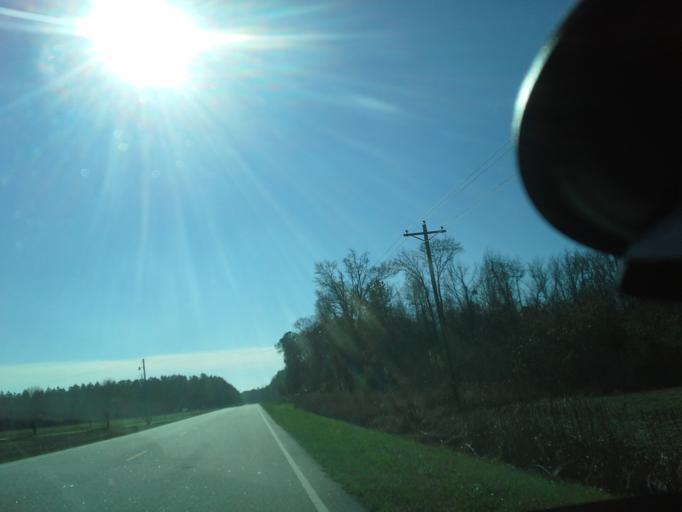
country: US
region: North Carolina
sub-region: Beaufort County
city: Belhaven
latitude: 35.5609
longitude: -76.6991
